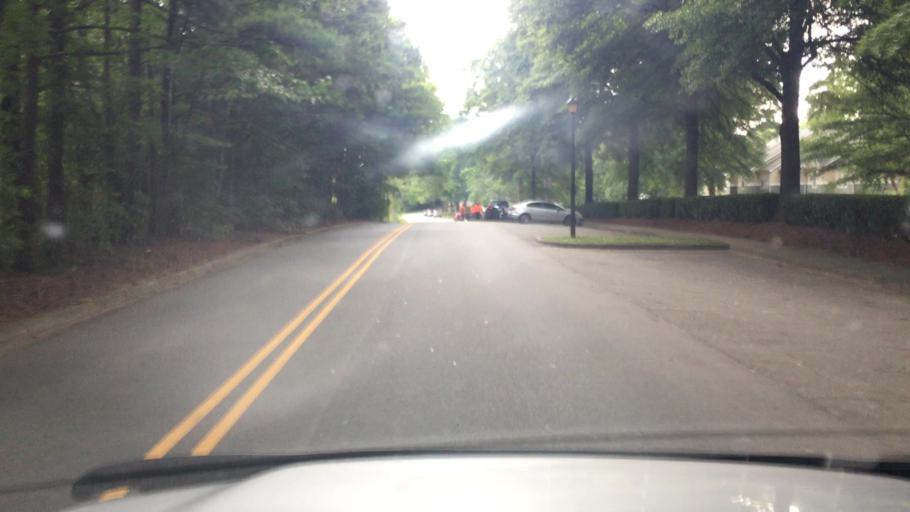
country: US
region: North Carolina
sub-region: Mecklenburg County
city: Cornelius
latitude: 35.4856
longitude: -80.8877
